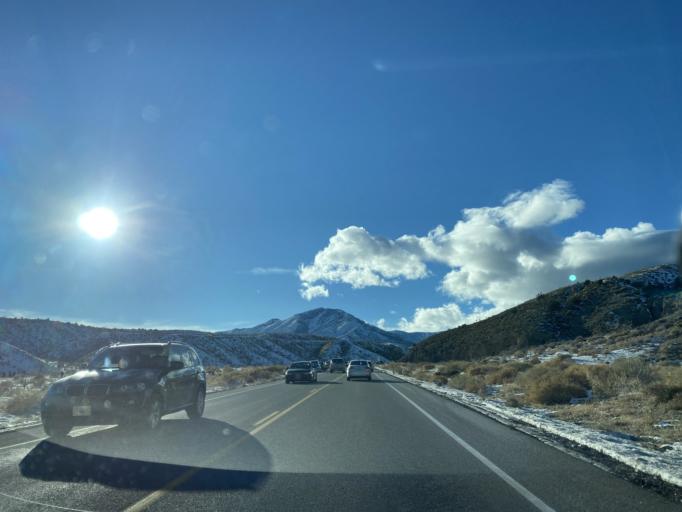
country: US
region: Nevada
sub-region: Clark County
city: Summerlin South
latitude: 36.2728
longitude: -115.5262
